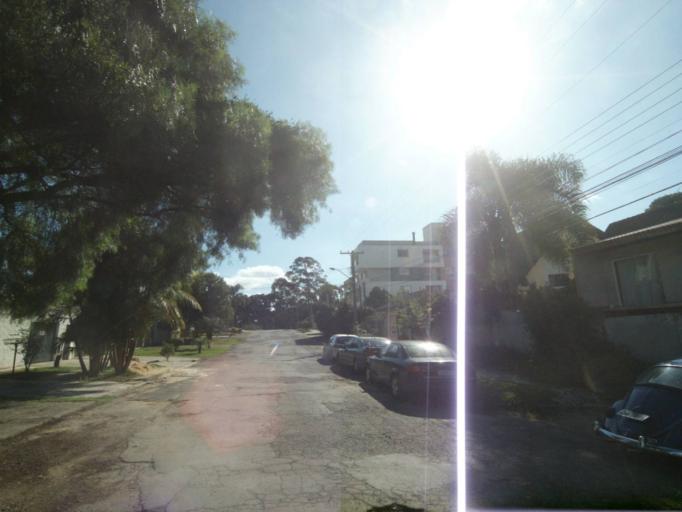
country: BR
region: Parana
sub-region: Curitiba
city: Curitiba
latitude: -25.4432
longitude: -49.3207
